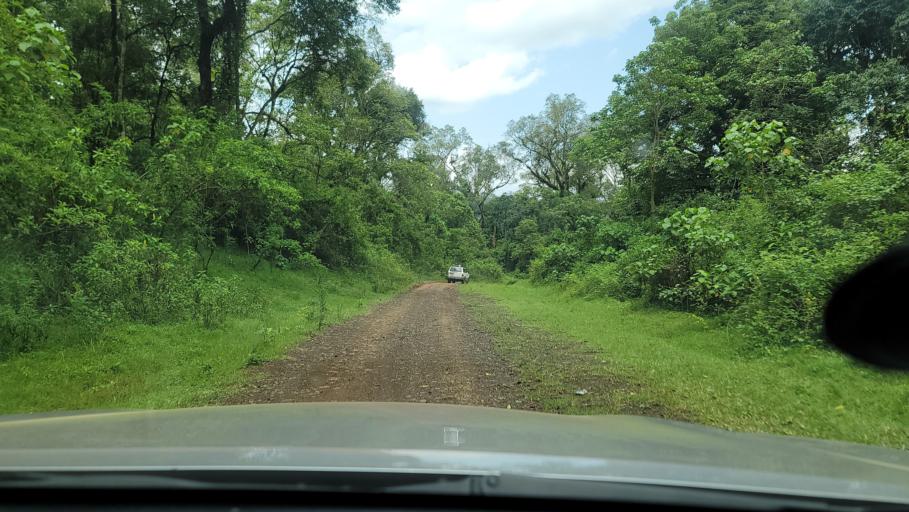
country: ET
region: Southern Nations, Nationalities, and People's Region
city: Bonga
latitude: 7.6500
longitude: 36.2468
